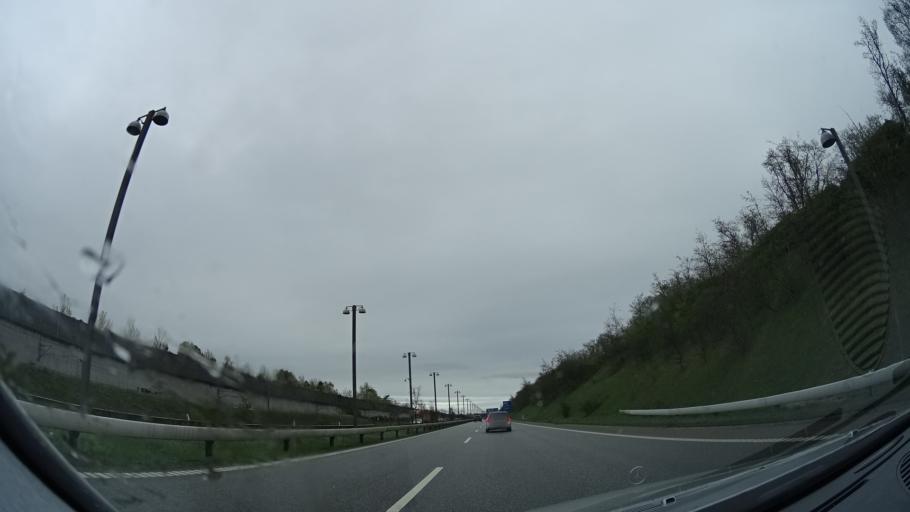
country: DK
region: Capital Region
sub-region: Tarnby Kommune
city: Tarnby
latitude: 55.6296
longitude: 12.6115
